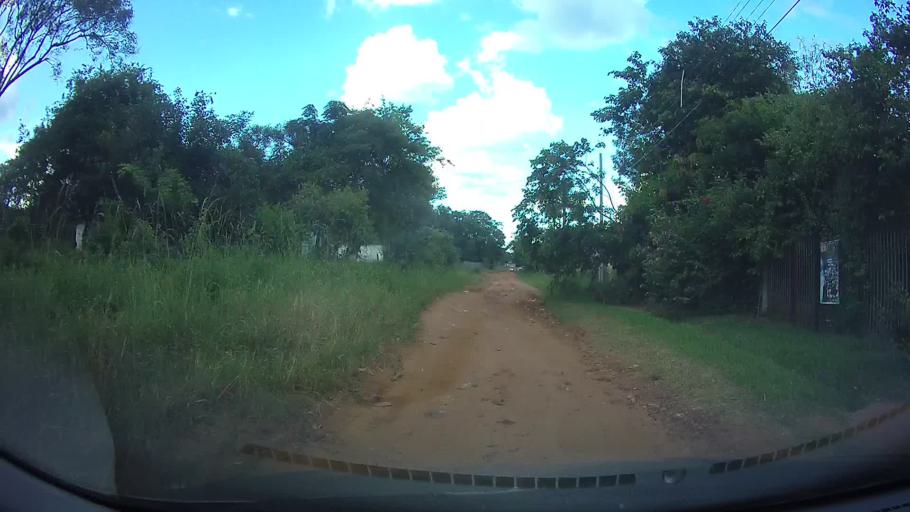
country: PY
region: Central
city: Limpio
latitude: -25.2516
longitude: -57.4588
